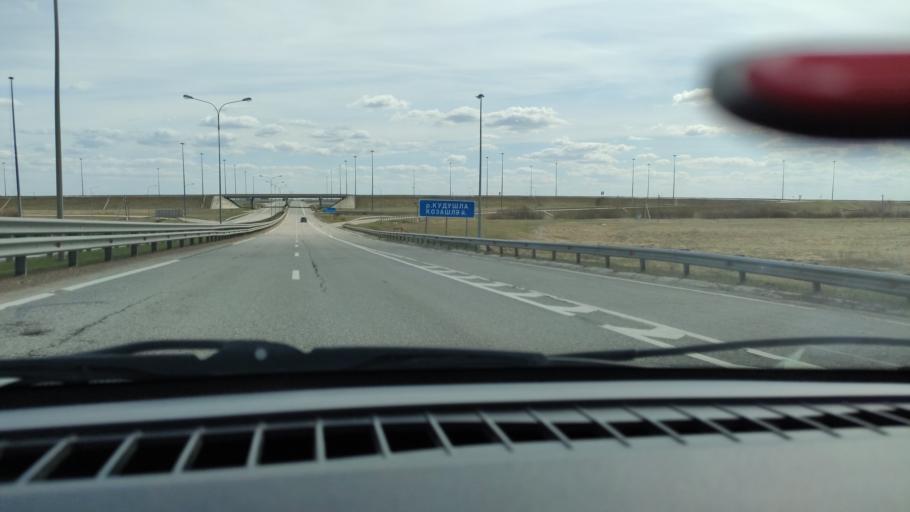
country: RU
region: Bashkortostan
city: Kushnarenkovo
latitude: 55.0773
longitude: 55.2775
